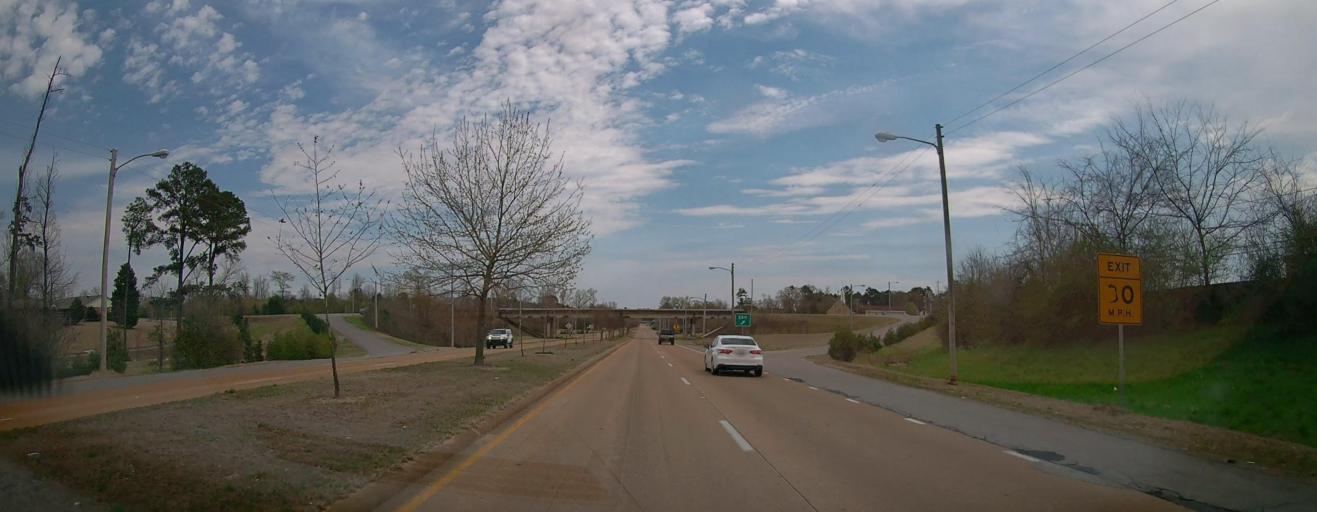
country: US
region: Mississippi
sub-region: Lee County
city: Tupelo
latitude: 34.2791
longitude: -88.7269
